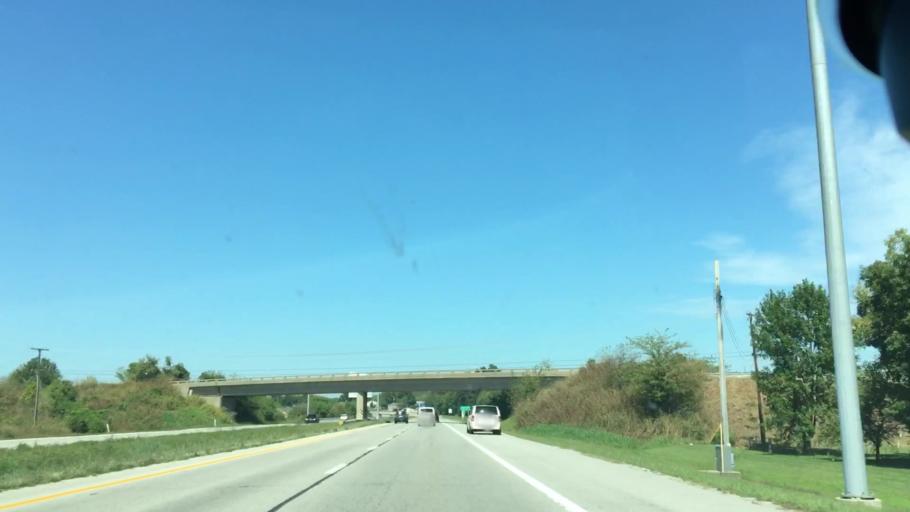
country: US
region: Kentucky
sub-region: Henderson County
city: Henderson
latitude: 37.8154
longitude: -87.5629
